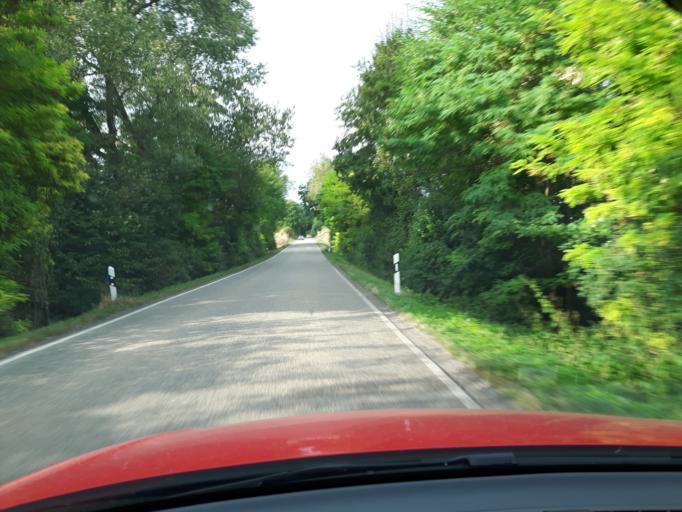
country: DE
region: Baden-Wuerttemberg
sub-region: Regierungsbezirk Stuttgart
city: Nordheim
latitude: 49.0959
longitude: 9.1025
